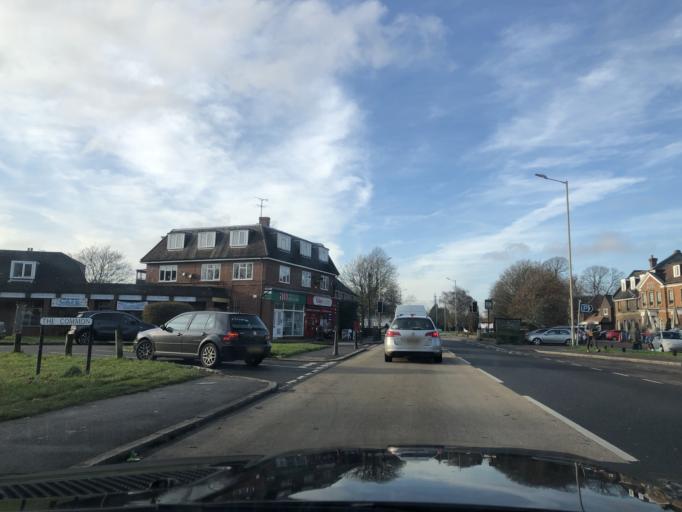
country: GB
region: England
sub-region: Buckinghamshire
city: Stokenchurch
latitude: 51.6600
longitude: -0.9013
